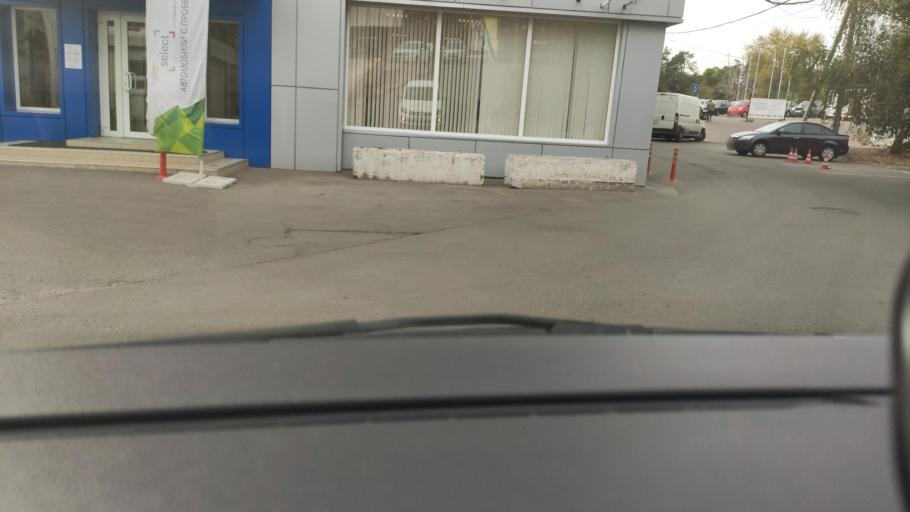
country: RU
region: Voronezj
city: Pridonskoy
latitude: 51.6464
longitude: 39.1093
